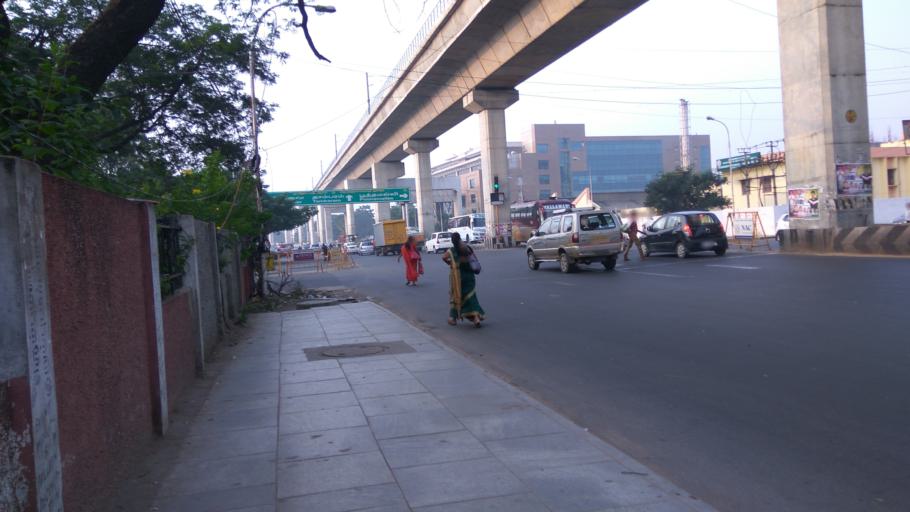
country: IN
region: Tamil Nadu
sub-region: Kancheepuram
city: Alandur
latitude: 13.0139
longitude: 80.2045
